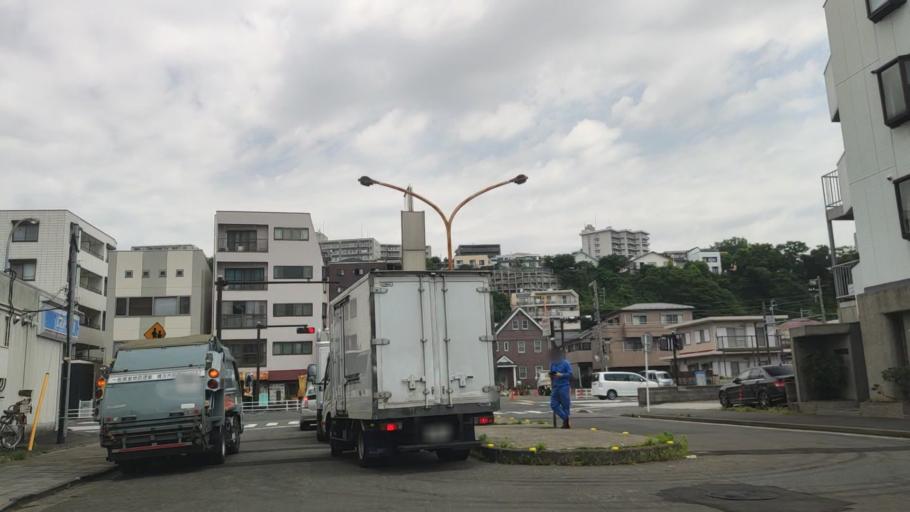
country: JP
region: Kanagawa
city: Yokohama
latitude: 35.4174
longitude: 139.6388
